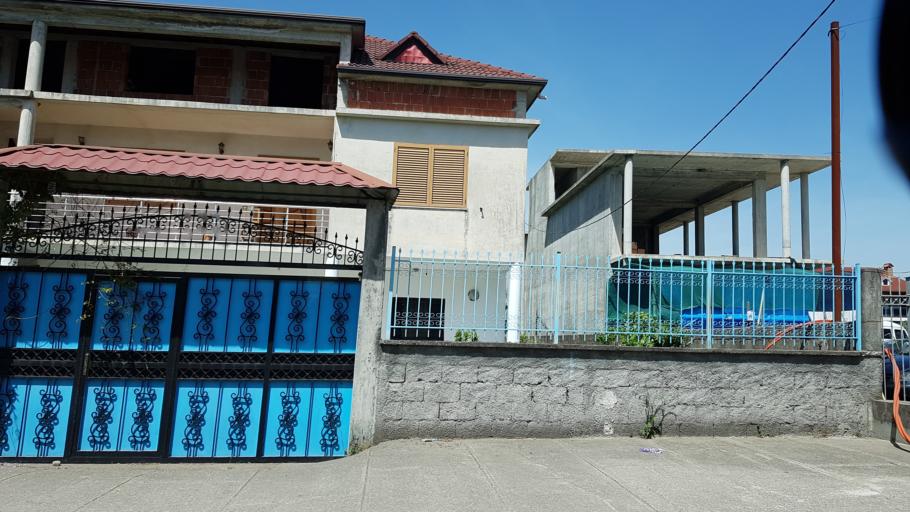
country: AL
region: Shkoder
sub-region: Rrethi i Shkodres
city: Shkoder
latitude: 42.0876
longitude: 19.5315
